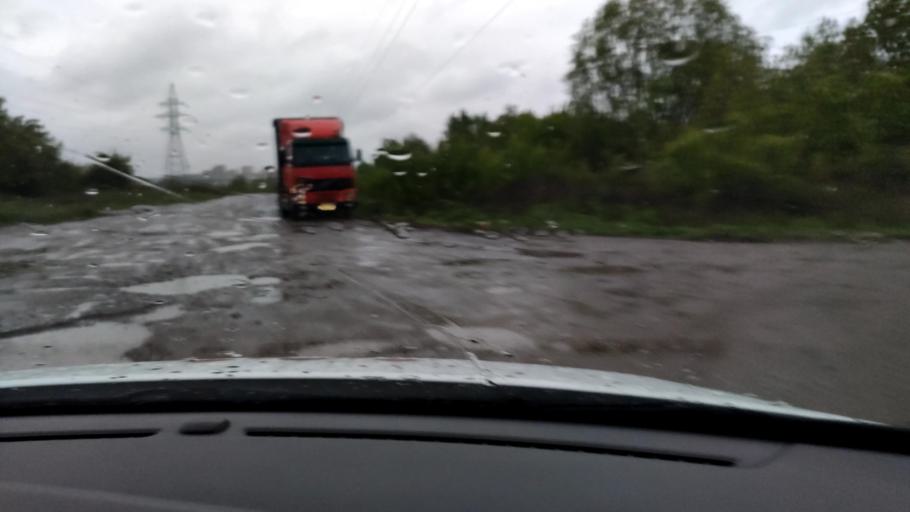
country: RU
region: Tatarstan
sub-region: Gorod Kazan'
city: Kazan
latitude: 55.7228
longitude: 49.1276
